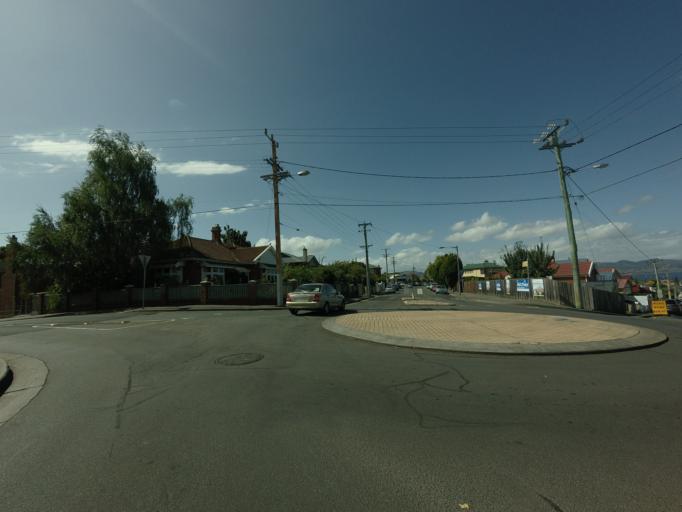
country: AU
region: Tasmania
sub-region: Hobart
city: Dynnyrne
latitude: -42.8986
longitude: 147.3172
